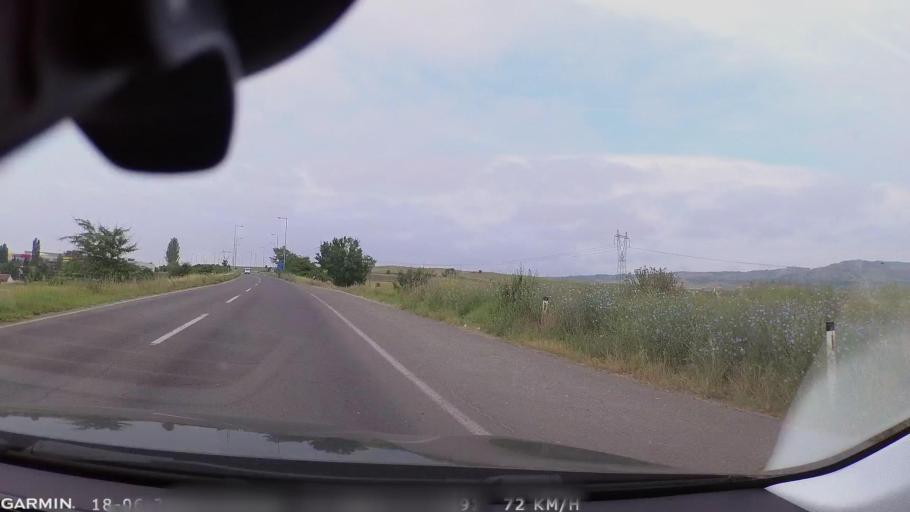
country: MK
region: Stip
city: Shtip
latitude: 41.7662
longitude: 22.1636
